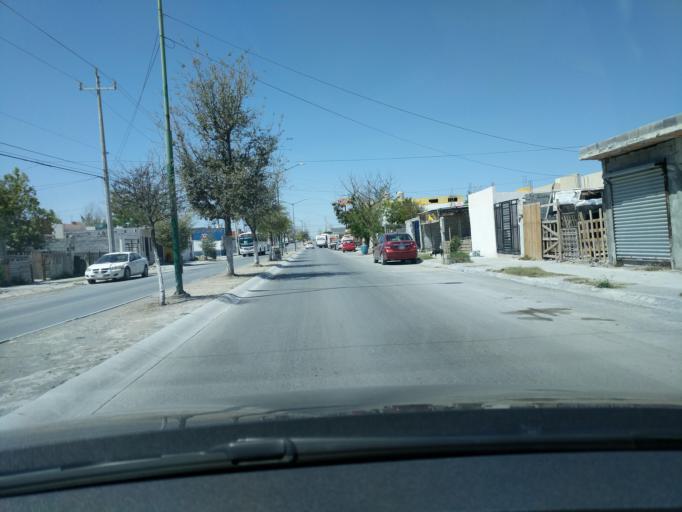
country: MX
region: Nuevo Leon
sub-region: Pesqueria
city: Colinas del Aeropuerto
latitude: 25.8240
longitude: -100.1197
